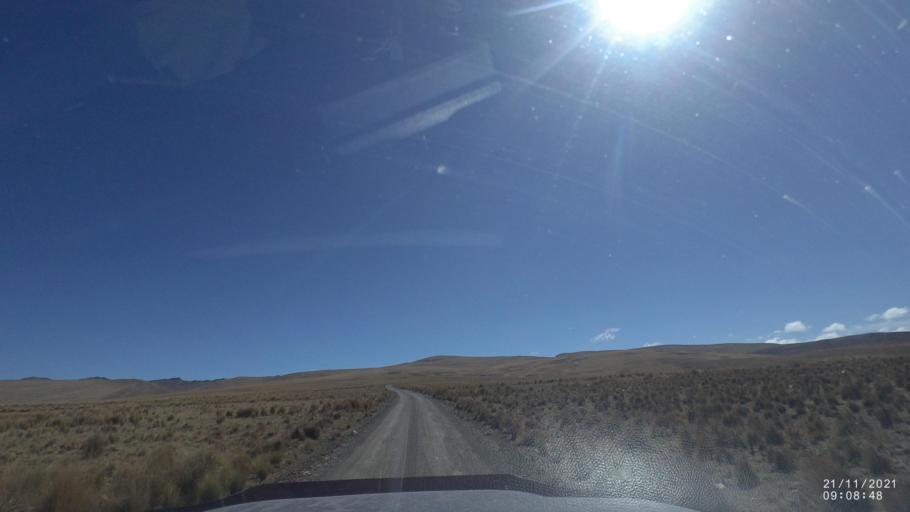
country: BO
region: Cochabamba
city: Cochabamba
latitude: -17.1608
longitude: -66.2657
